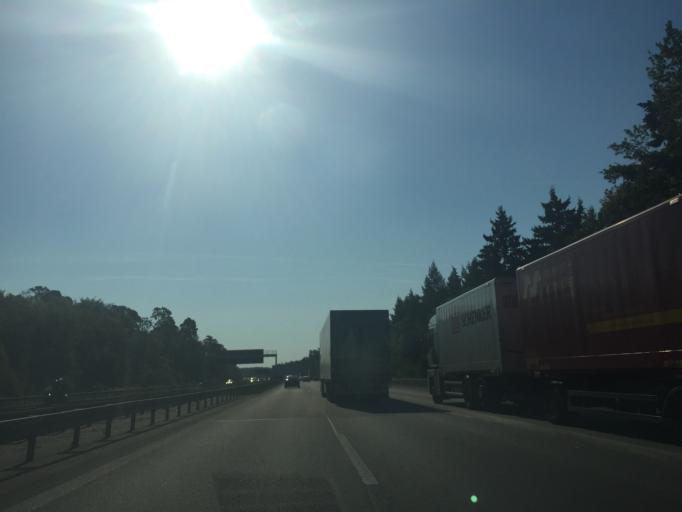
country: DE
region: Baden-Wuerttemberg
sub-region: Karlsruhe Region
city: Sankt Leon-Rot
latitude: 49.2751
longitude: 8.6376
